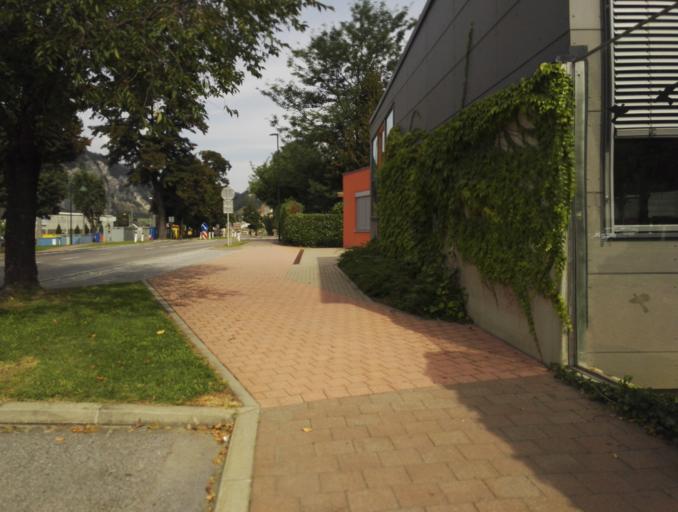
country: AT
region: Styria
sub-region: Politischer Bezirk Graz-Umgebung
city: Peggau
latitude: 47.2077
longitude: 15.3440
